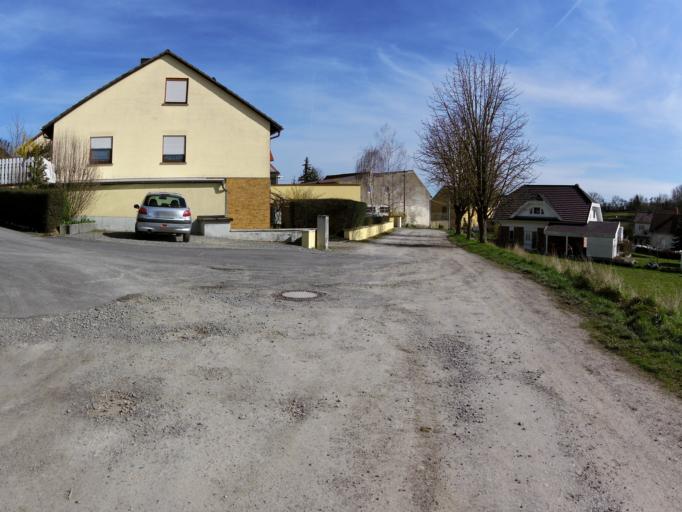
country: DE
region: Bavaria
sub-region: Regierungsbezirk Unterfranken
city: Buchbrunn
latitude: 49.7503
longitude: 10.1192
